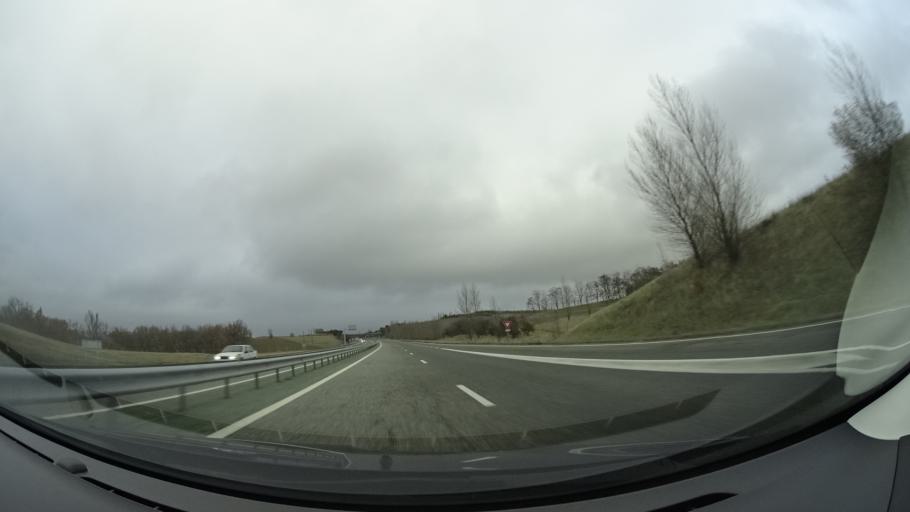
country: FR
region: Midi-Pyrenees
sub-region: Departement de la Haute-Garonne
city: Nailloux
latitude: 43.3862
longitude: 1.6235
